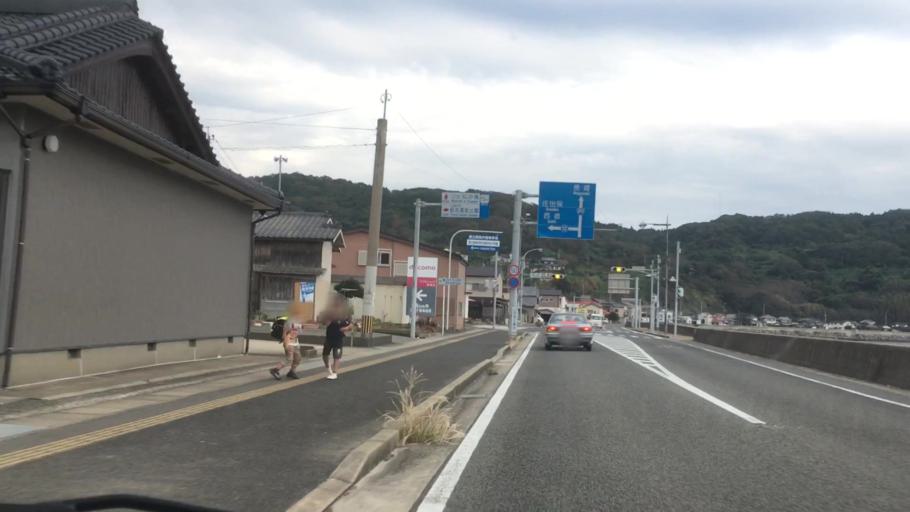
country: JP
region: Nagasaki
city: Togitsu
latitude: 32.9326
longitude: 129.6460
